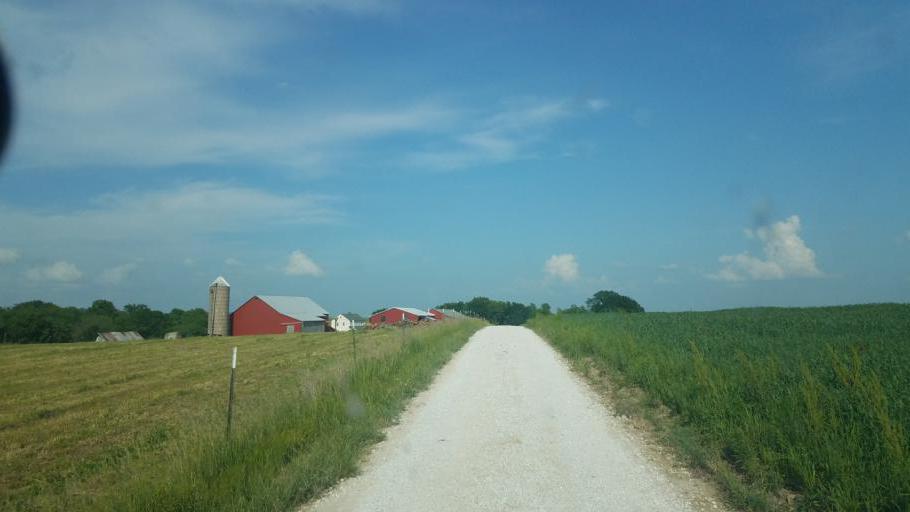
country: US
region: Missouri
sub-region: Cooper County
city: Boonville
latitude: 38.8560
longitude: -92.6489
